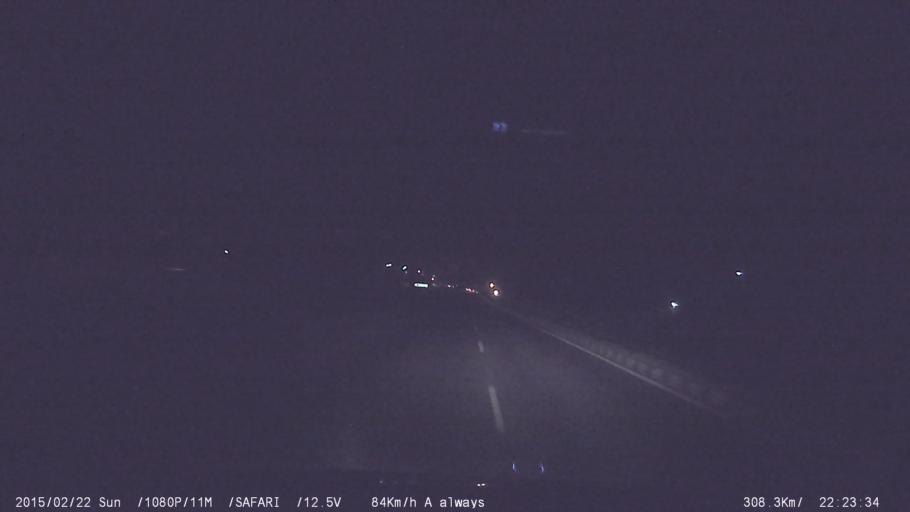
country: IN
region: Tamil Nadu
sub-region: Karur
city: Karur
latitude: 11.0270
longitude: 78.0655
